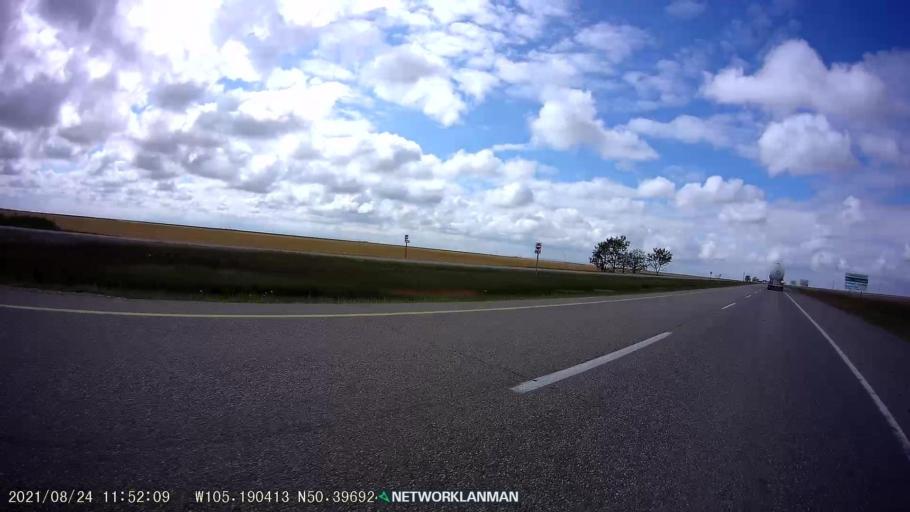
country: CA
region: Saskatchewan
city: Moose Jaw
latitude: 50.3975
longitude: -105.1909
